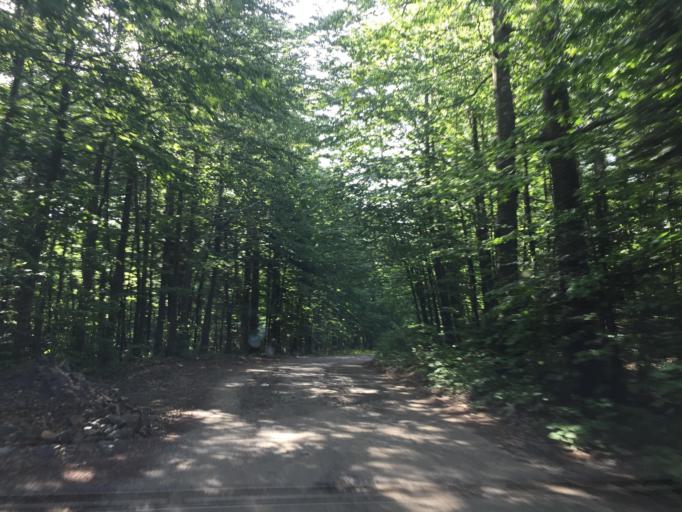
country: HR
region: Primorsko-Goranska
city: Podhum
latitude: 45.4430
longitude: 14.5582
